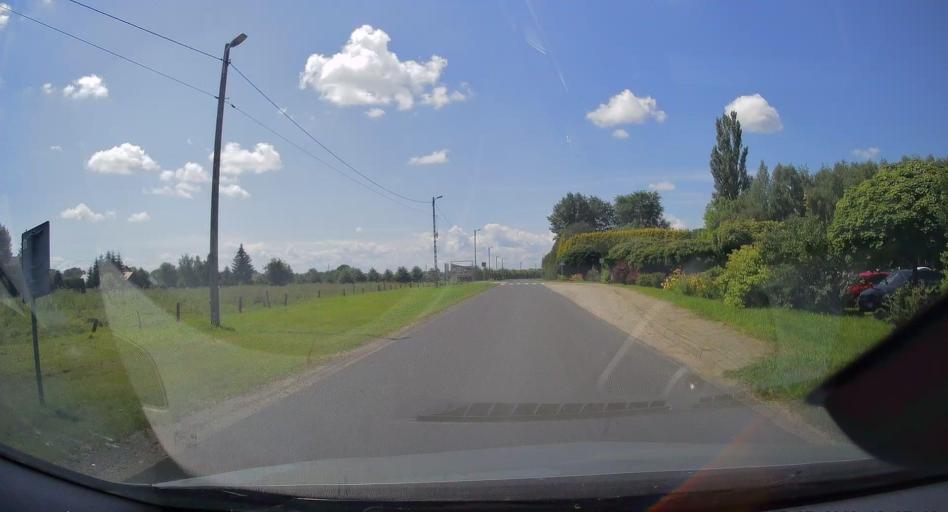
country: PL
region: Subcarpathian Voivodeship
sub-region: Powiat przemyski
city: Medyka
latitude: 49.8182
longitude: 22.8636
